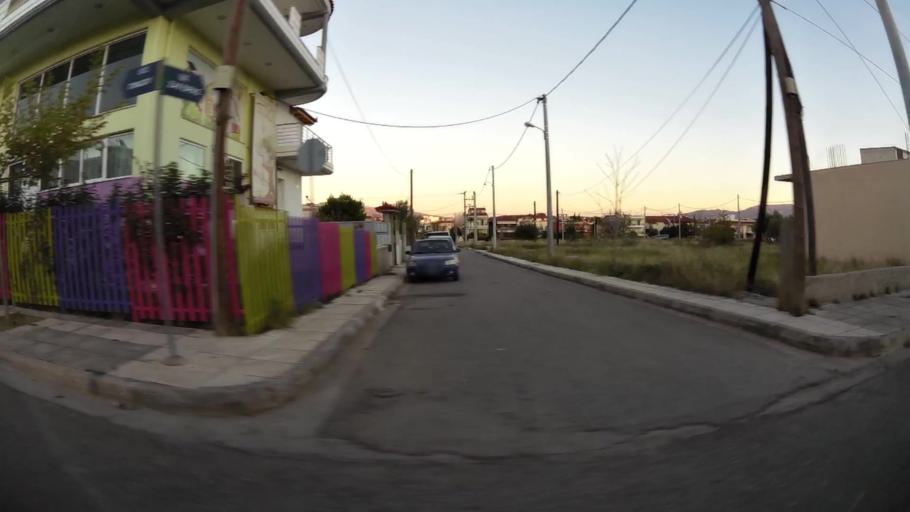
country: GR
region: Attica
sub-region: Nomarchia Dytikis Attikis
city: Ano Liosia
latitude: 38.0882
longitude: 23.7091
